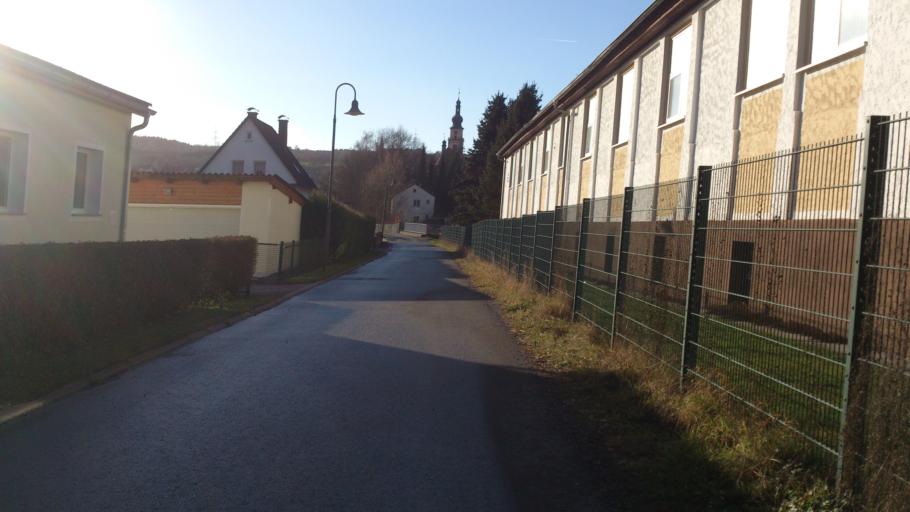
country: DE
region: Bavaria
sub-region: Upper Franconia
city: Stadtsteinach
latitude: 50.1628
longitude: 11.5110
